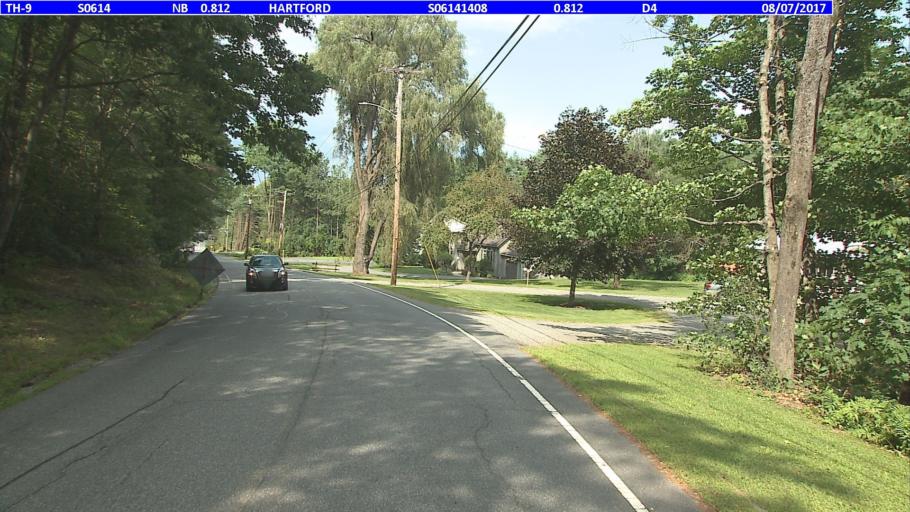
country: US
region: Vermont
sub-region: Windsor County
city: White River Junction
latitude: 43.6660
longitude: -72.3265
